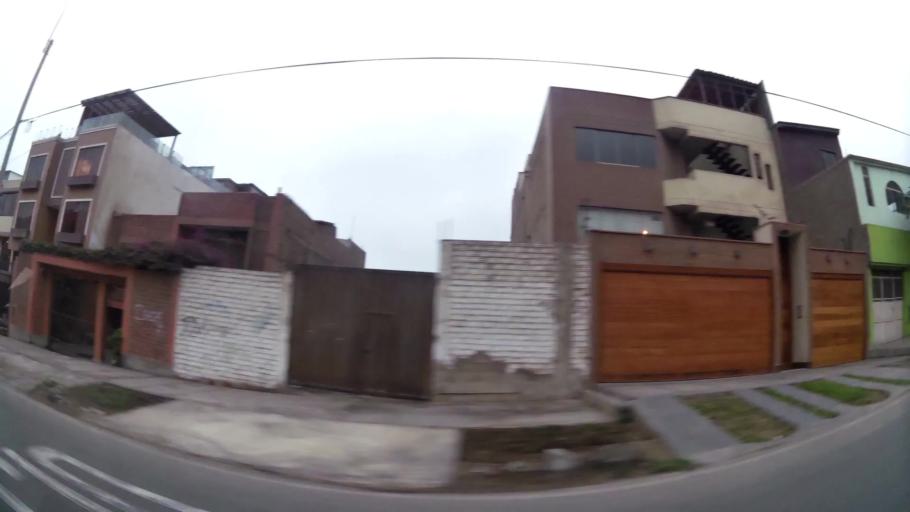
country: PE
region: Lima
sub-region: Lima
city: La Molina
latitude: -12.1143
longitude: -76.9407
